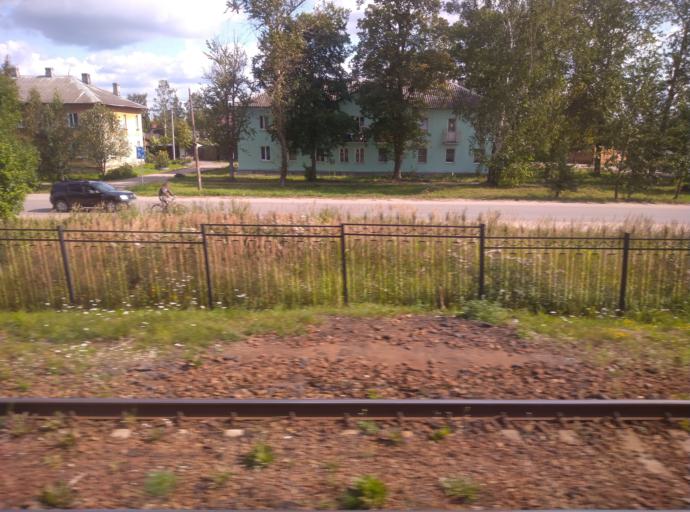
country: RU
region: Leningrad
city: Ul'yanovka
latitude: 59.6347
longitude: 30.7589
